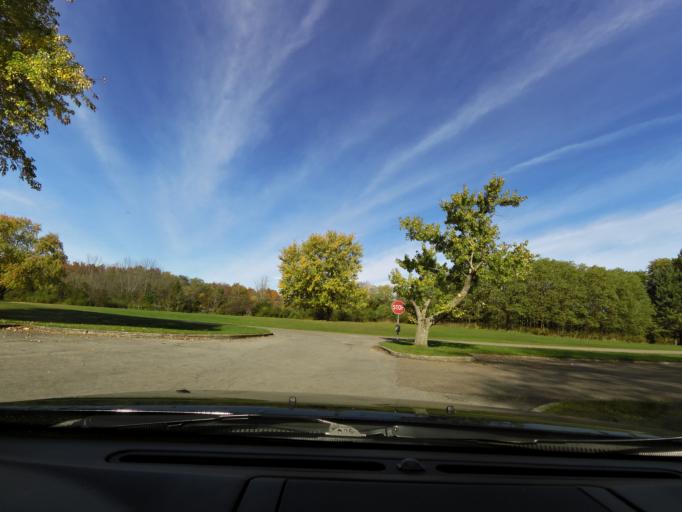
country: US
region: New York
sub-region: Livingston County
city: Mount Morris
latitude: 42.7354
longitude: -77.9077
